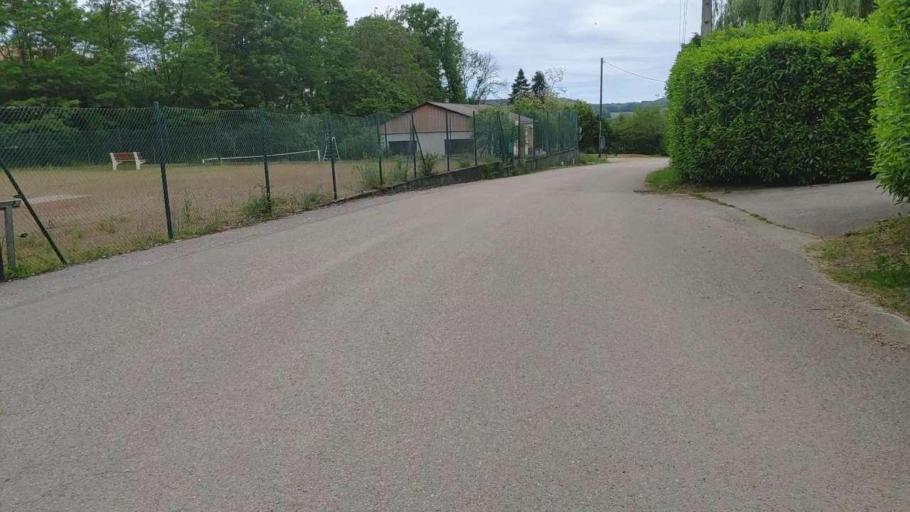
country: FR
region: Franche-Comte
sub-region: Departement du Jura
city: Montmorot
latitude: 46.7541
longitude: 5.5612
